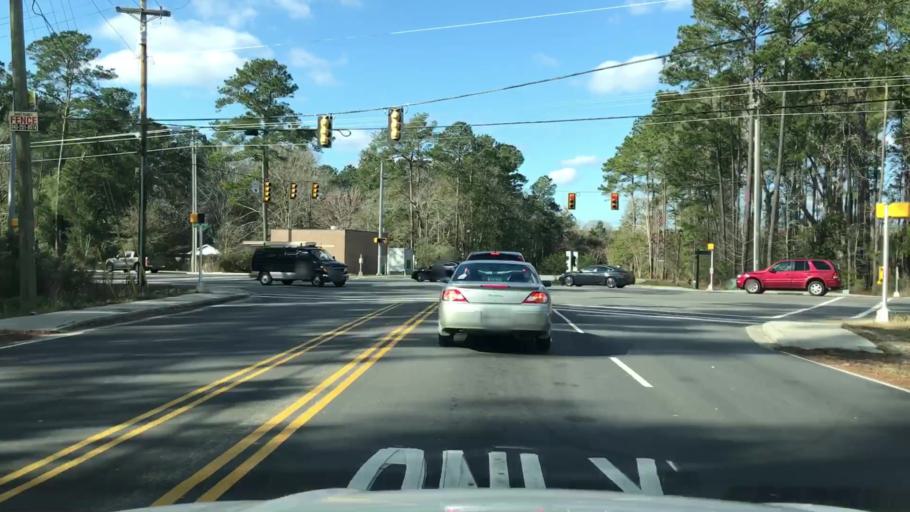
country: US
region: South Carolina
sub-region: Horry County
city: Socastee
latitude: 33.6601
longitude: -79.0122
